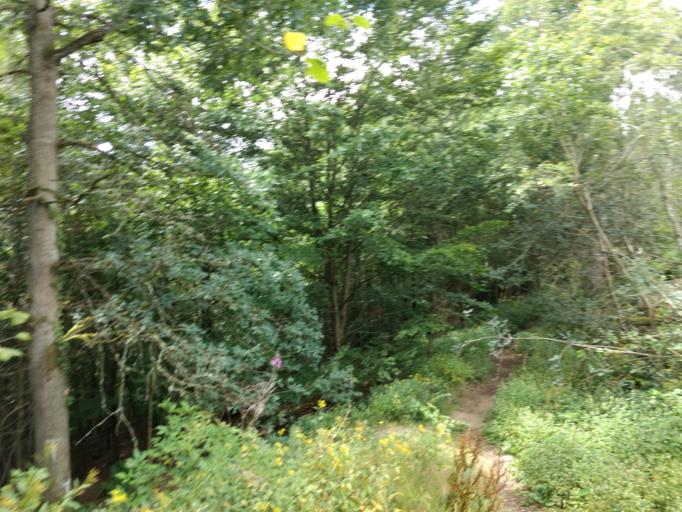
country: BE
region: Wallonia
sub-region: Province du Luxembourg
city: Houffalize
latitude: 50.1426
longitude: 5.7350
